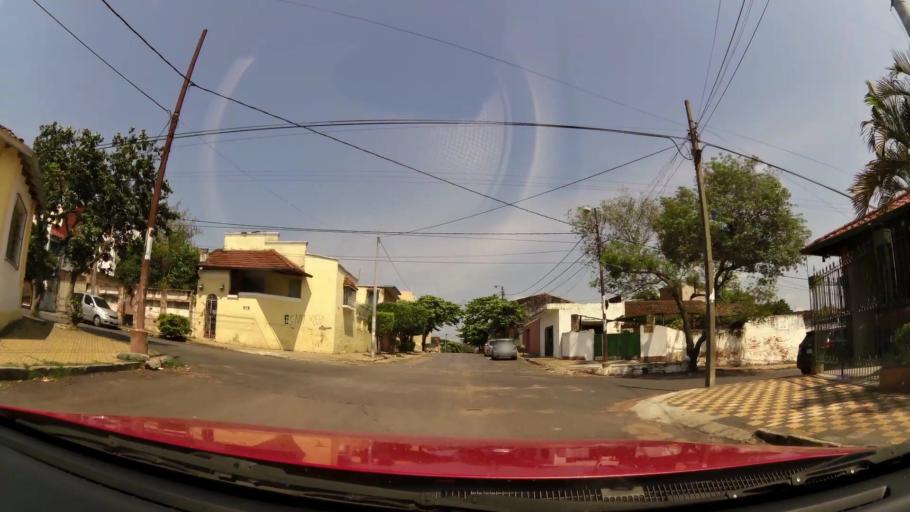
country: PY
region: Presidente Hayes
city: Nanawa
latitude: -25.2783
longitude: -57.6553
